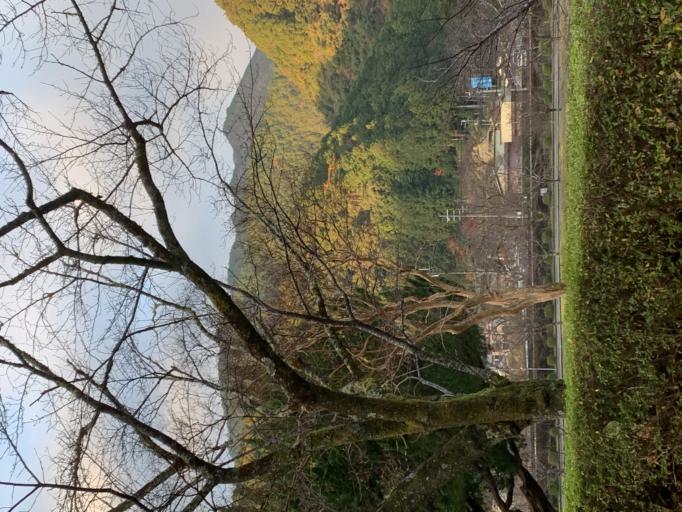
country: JP
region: Mie
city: Owase
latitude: 34.0438
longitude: 135.9601
